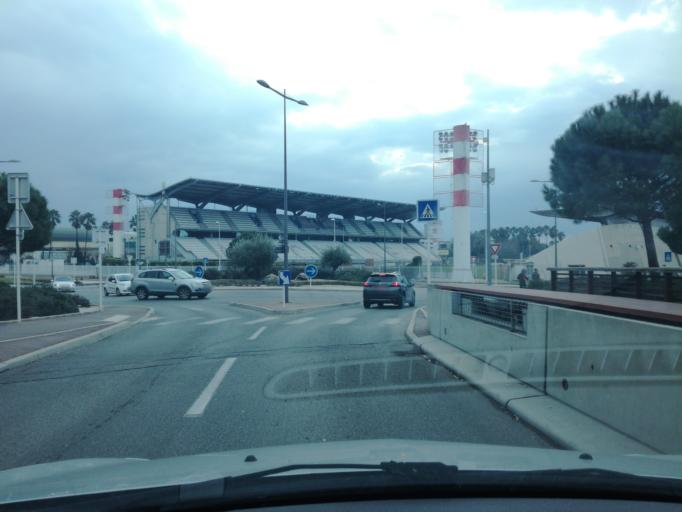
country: FR
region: Provence-Alpes-Cote d'Azur
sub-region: Departement des Alpes-Maritimes
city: Mandelieu-la-Napoule
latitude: 43.5542
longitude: 6.9638
